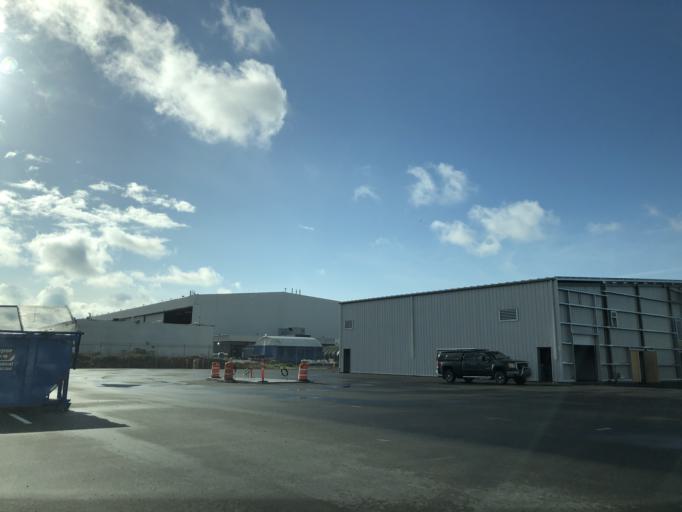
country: CA
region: British Columbia
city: Richmond
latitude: 49.1975
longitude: -123.1621
